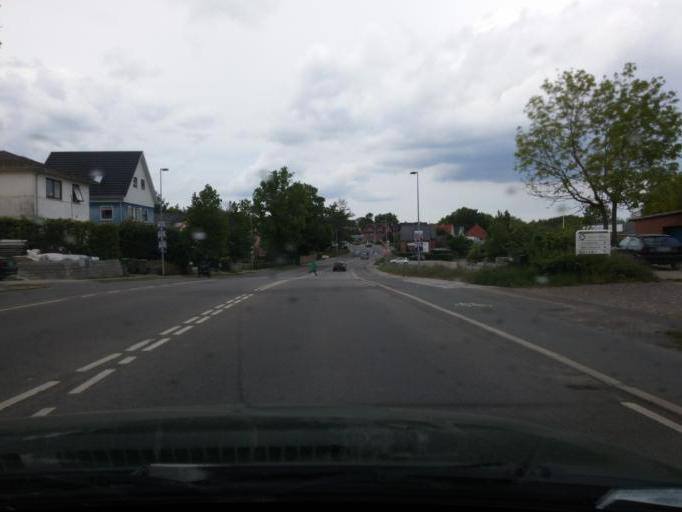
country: DK
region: South Denmark
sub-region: Odense Kommune
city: Odense
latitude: 55.4018
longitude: 10.3567
